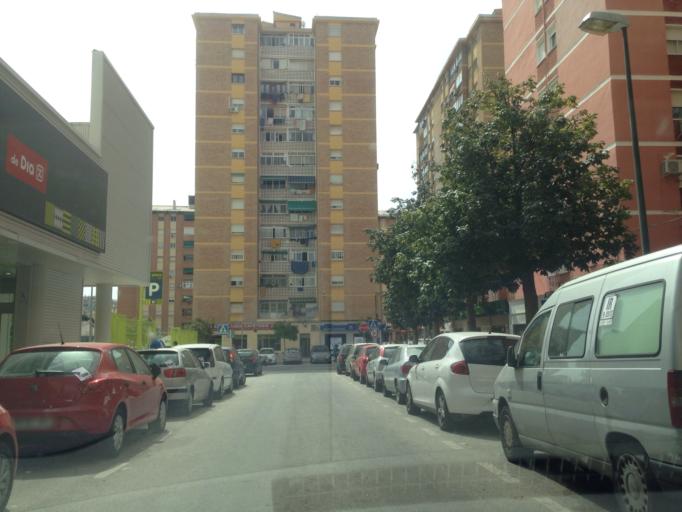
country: ES
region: Andalusia
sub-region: Provincia de Malaga
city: Malaga
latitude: 36.7095
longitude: -4.4414
